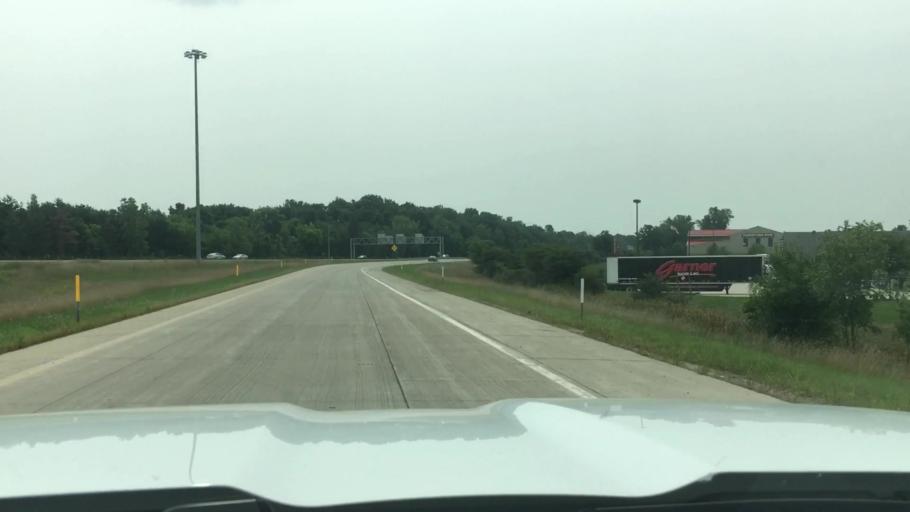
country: US
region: Michigan
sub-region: Eaton County
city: Waverly
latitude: 42.7388
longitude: -84.6696
